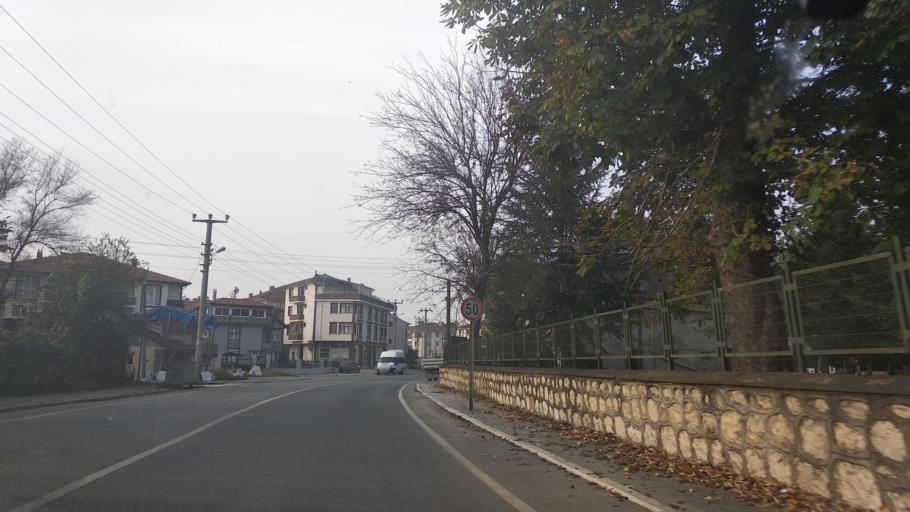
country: TR
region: Duzce
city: Duzce
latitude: 40.8289
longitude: 31.1724
